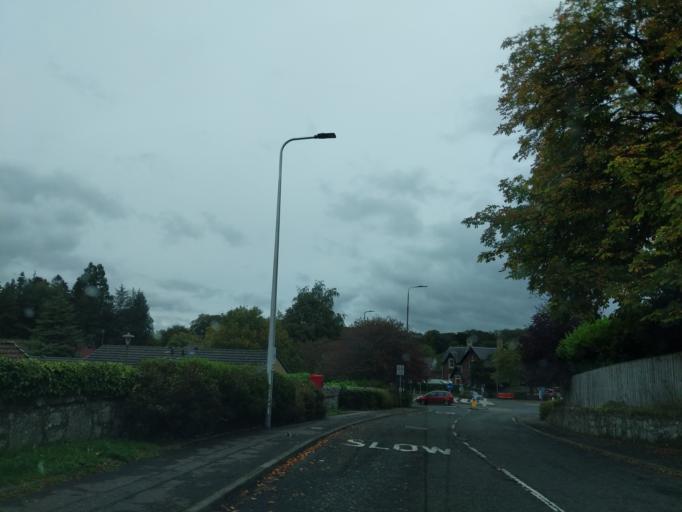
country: GB
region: Scotland
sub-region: Edinburgh
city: Balerno
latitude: 55.8845
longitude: -3.3417
